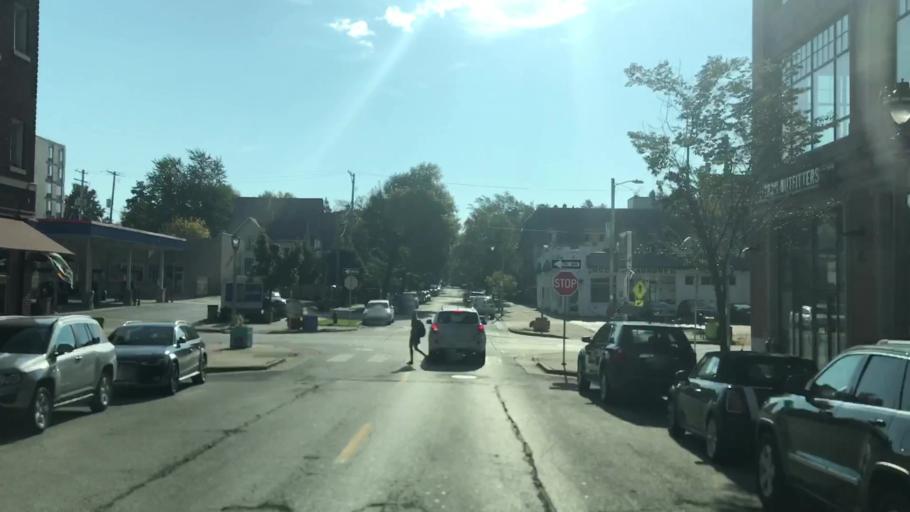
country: US
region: Wisconsin
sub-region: Milwaukee County
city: Milwaukee
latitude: 43.0589
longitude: -87.8855
